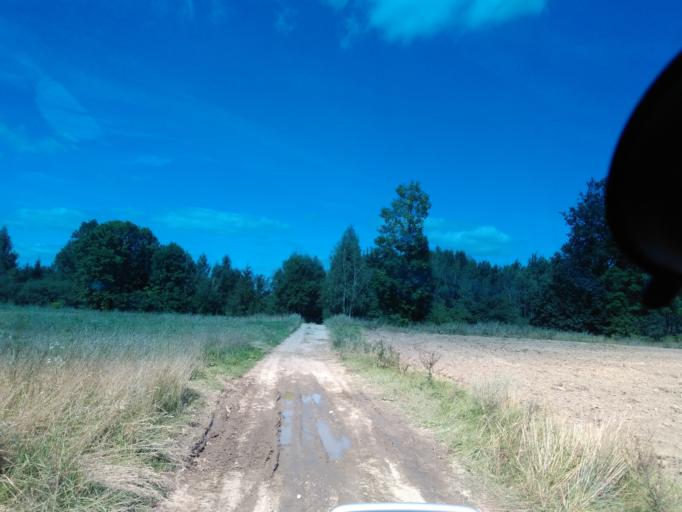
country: BY
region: Minsk
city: Stan'kava
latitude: 53.6262
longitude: 27.3143
